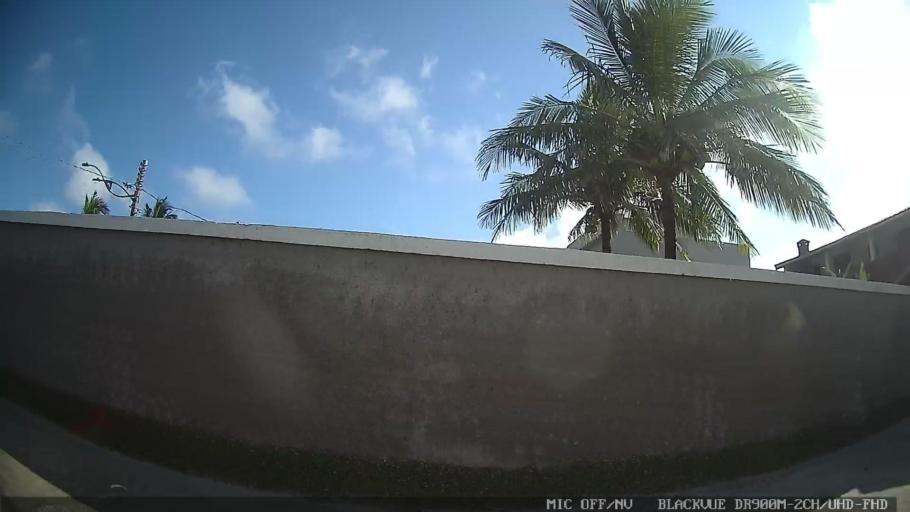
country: BR
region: Sao Paulo
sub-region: Peruibe
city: Peruibe
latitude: -24.2947
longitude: -46.9615
